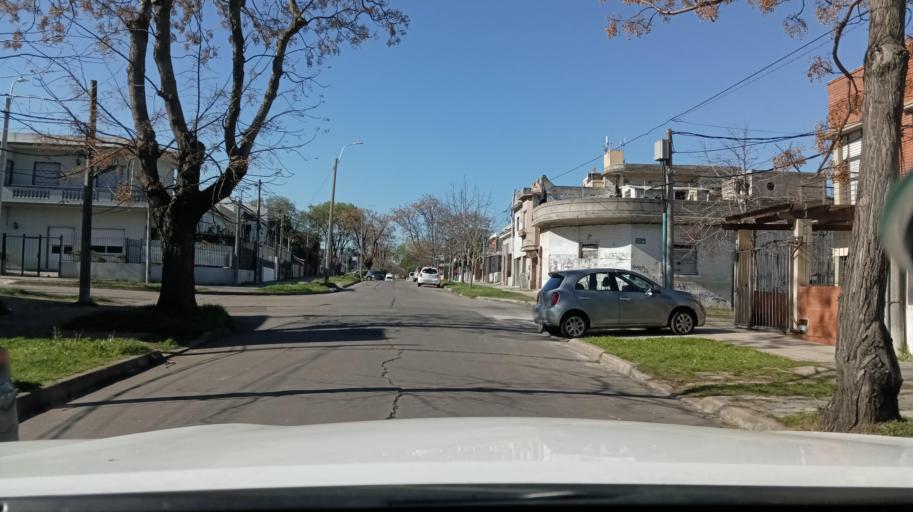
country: UY
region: Montevideo
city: Montevideo
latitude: -34.8926
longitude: -56.1233
